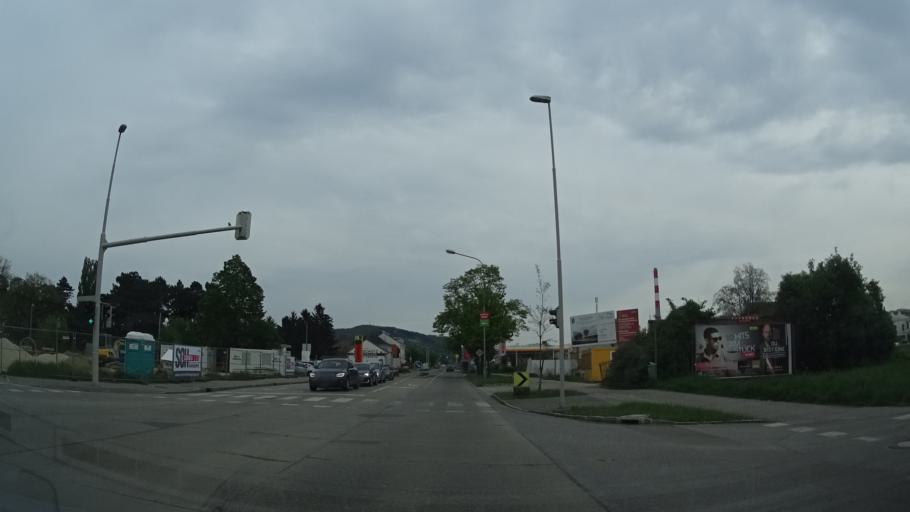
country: AT
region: Lower Austria
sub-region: Politischer Bezirk Korneuburg
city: Korneuburg
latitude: 48.3405
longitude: 16.3367
